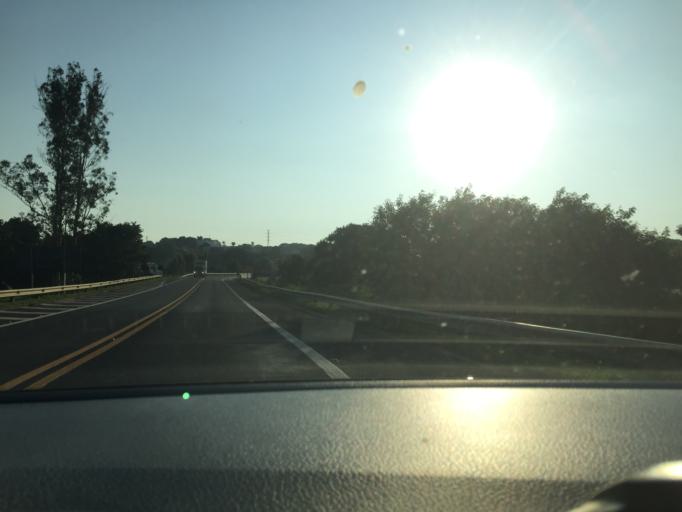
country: BR
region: Sao Paulo
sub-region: Louveira
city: Louveira
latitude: -23.0884
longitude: -46.9469
